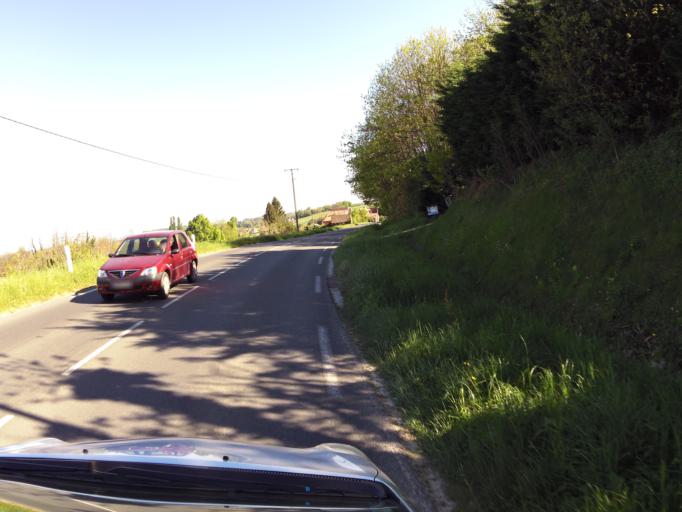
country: FR
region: Aquitaine
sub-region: Departement de la Dordogne
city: Sarlat-la-Caneda
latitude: 44.9269
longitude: 1.2068
